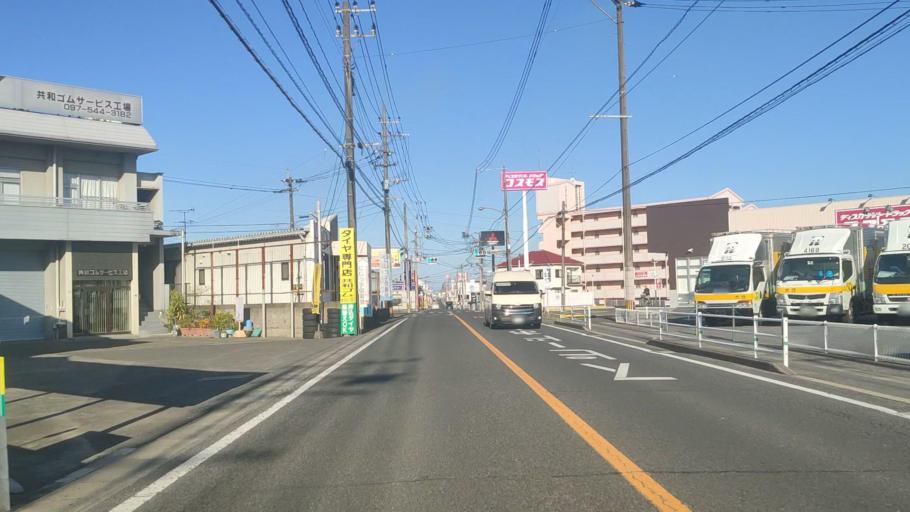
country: JP
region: Oita
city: Oita
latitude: 33.2101
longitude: 131.6065
